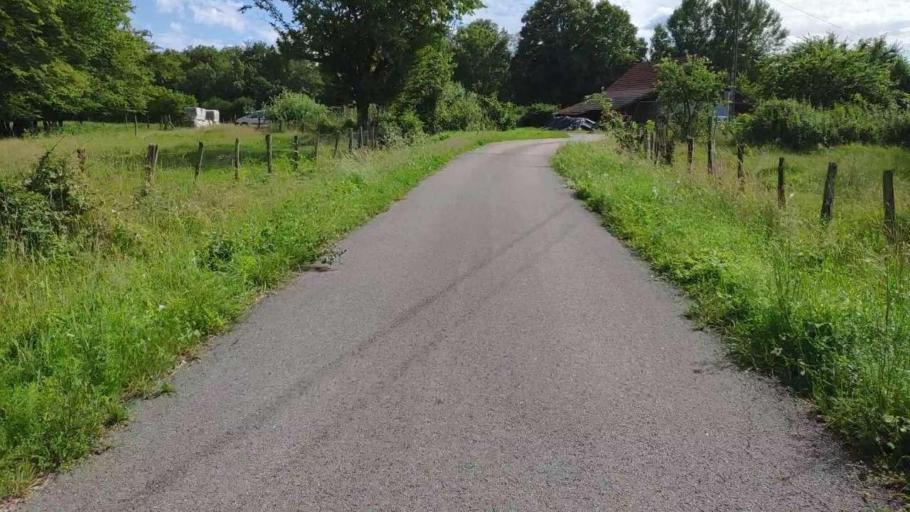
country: FR
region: Franche-Comte
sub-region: Departement du Jura
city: Bletterans
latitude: 46.8055
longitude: 5.4746
